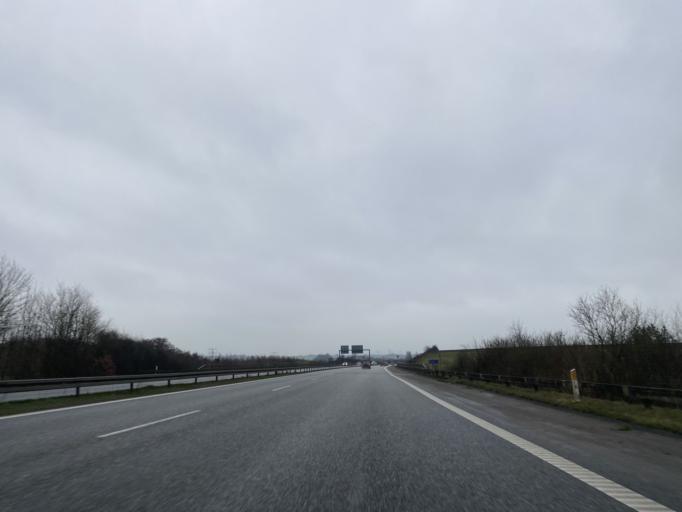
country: DK
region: Central Jutland
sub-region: Arhus Kommune
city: Framlev
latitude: 56.1492
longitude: 10.0442
